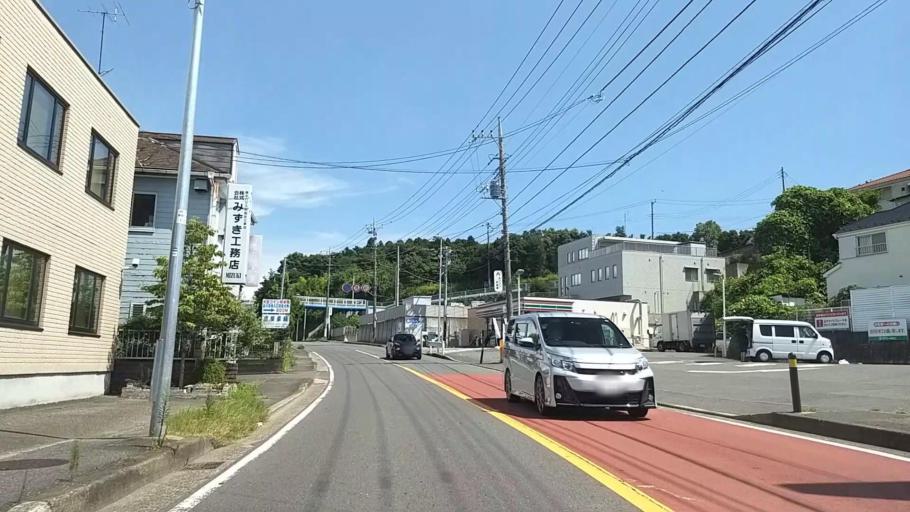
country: JP
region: Kanagawa
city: Fujisawa
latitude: 35.3730
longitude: 139.5101
